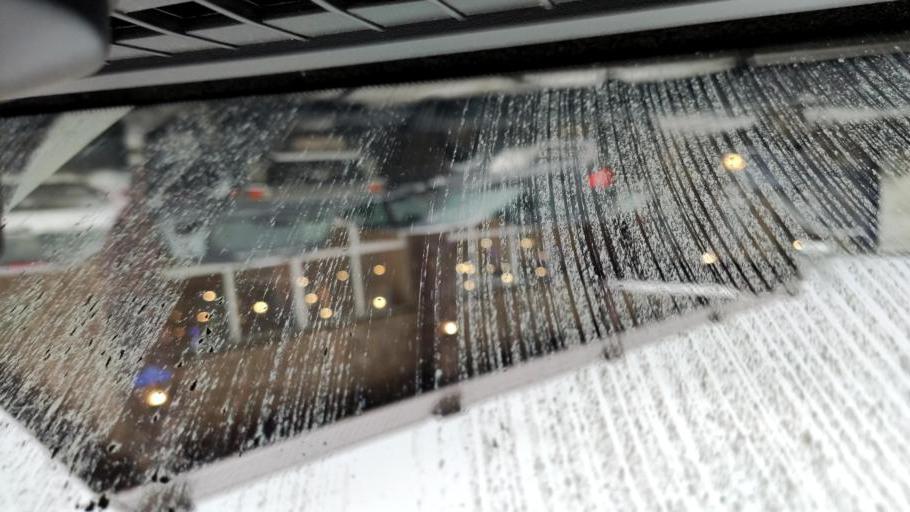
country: RU
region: Perm
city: Kondratovo
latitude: 57.9560
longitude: 56.1282
